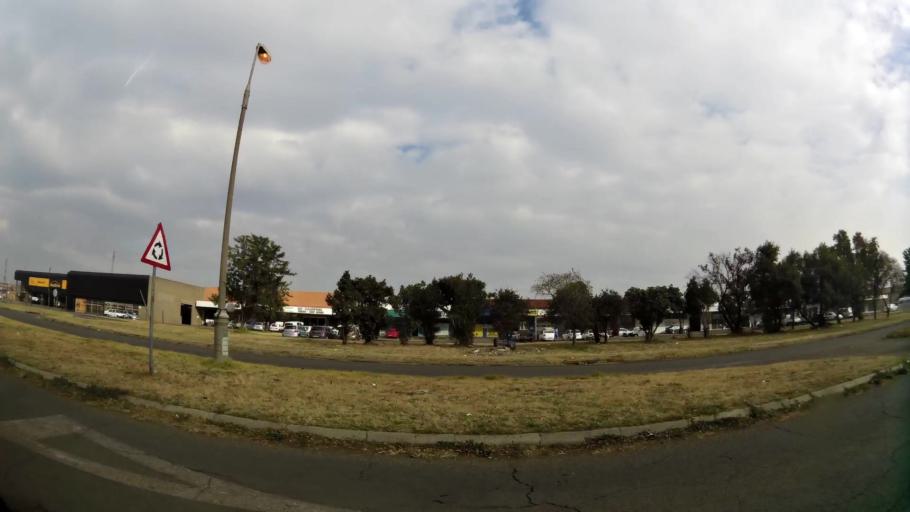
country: ZA
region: Gauteng
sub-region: Sedibeng District Municipality
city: Vanderbijlpark
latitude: -26.6965
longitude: 27.8404
